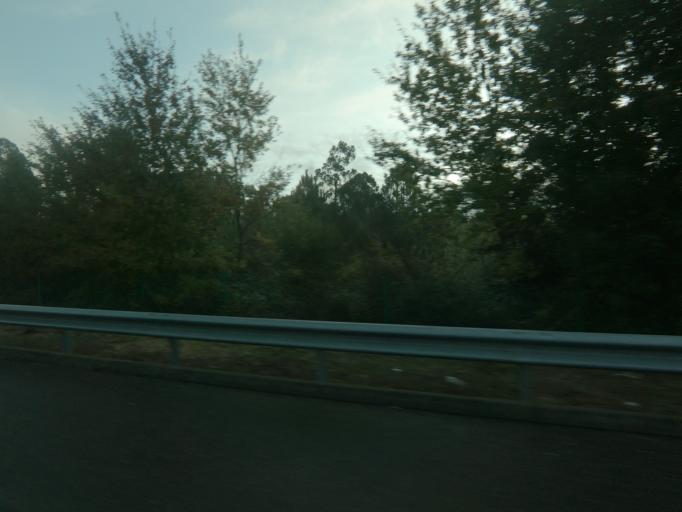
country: ES
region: Galicia
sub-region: Provincia de Pontevedra
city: Tui
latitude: 42.0698
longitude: -8.6398
